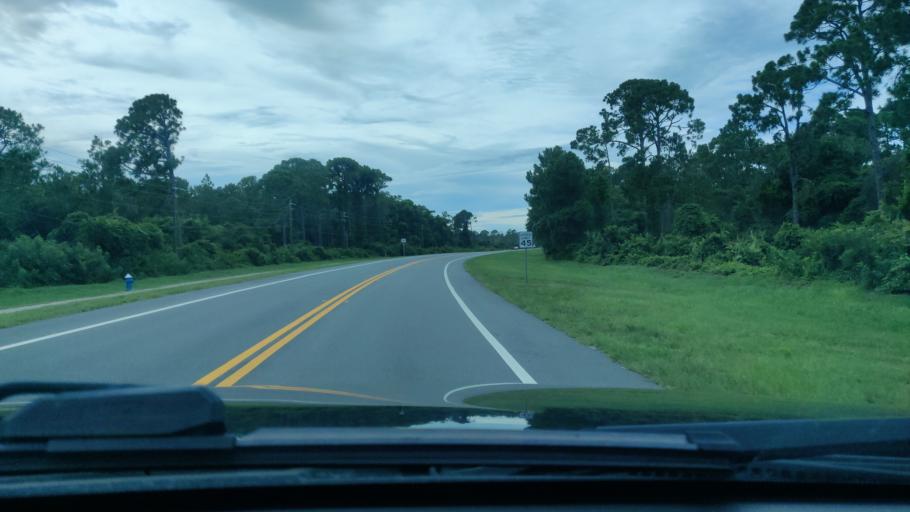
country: US
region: Florida
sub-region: Flagler County
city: Palm Coast
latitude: 29.5370
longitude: -81.1737
